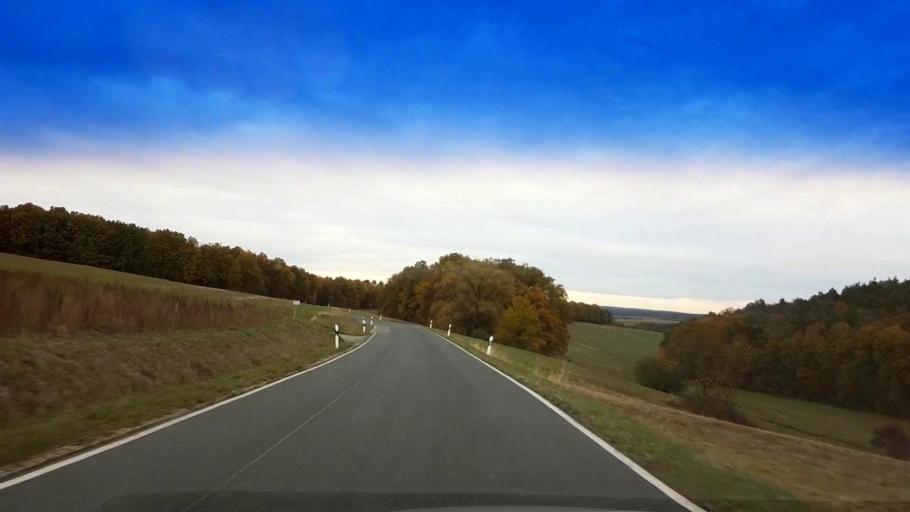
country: DE
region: Bavaria
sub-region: Upper Franconia
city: Priesendorf
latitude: 49.9355
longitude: 10.6937
